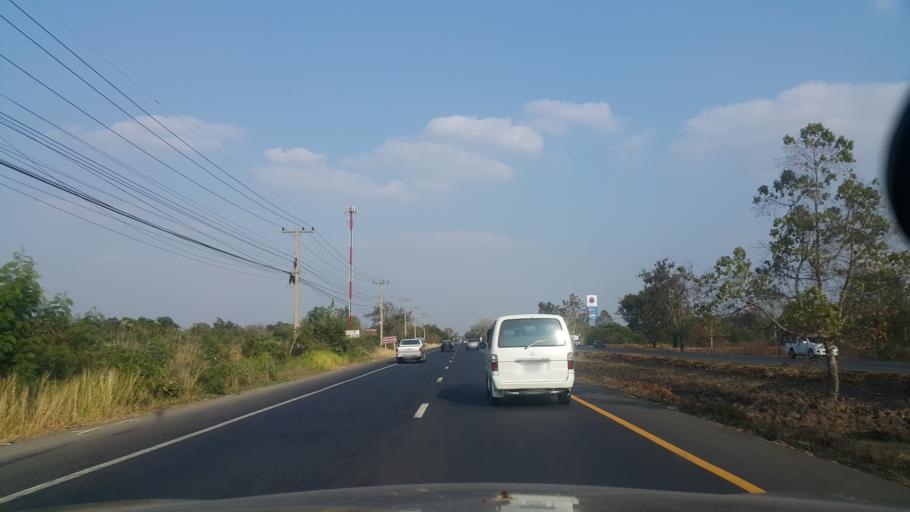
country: TH
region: Buriram
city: Nang Rong
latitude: 14.6351
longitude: 102.7417
